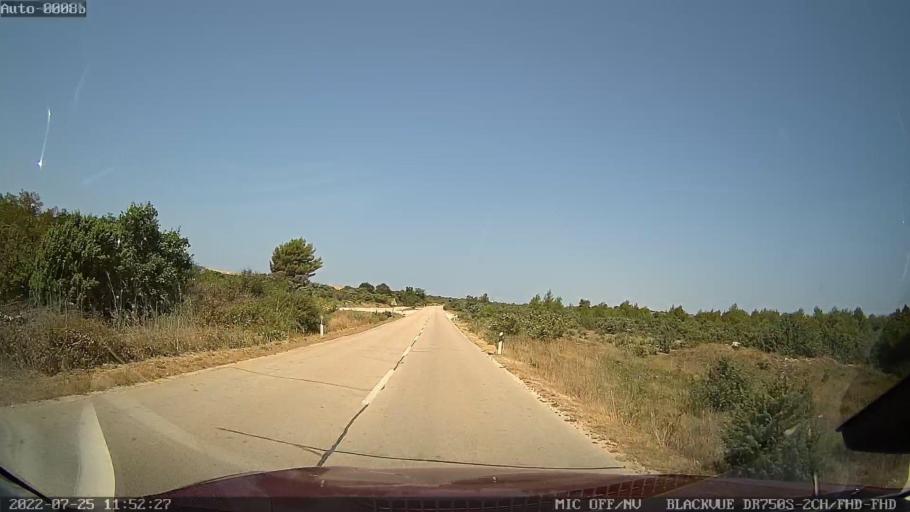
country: HR
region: Zadarska
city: Vrsi
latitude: 44.2479
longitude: 15.2441
